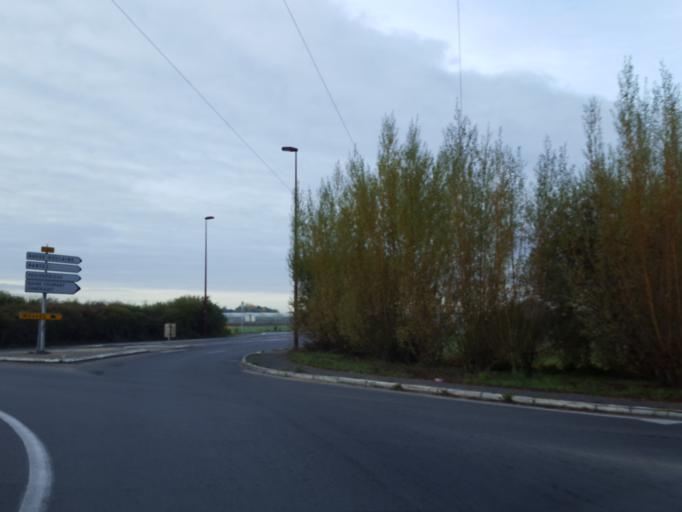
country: FR
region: Pays de la Loire
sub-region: Departement de la Loire-Atlantique
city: Saint-Julien-de-Concelles
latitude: 47.2554
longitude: -1.4103
